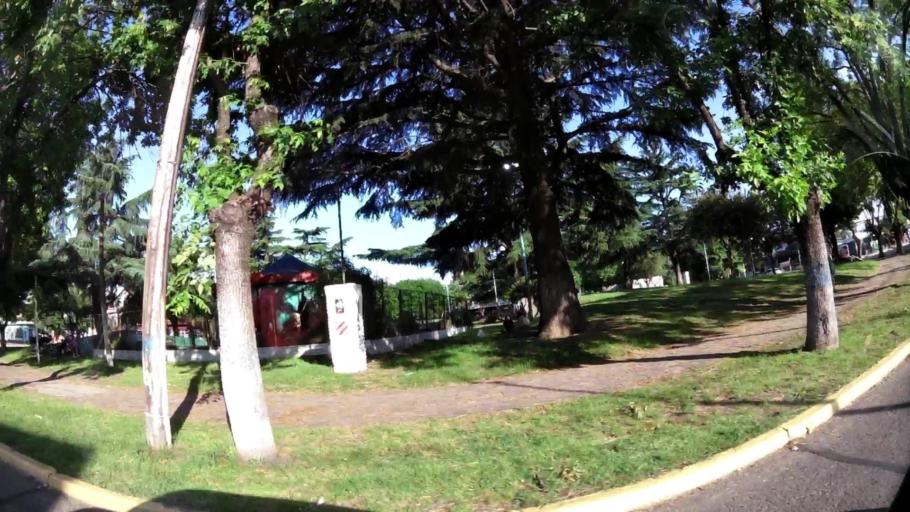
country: AR
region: Buenos Aires
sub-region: Partido de Merlo
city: Merlo
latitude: -34.6827
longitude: -58.7292
